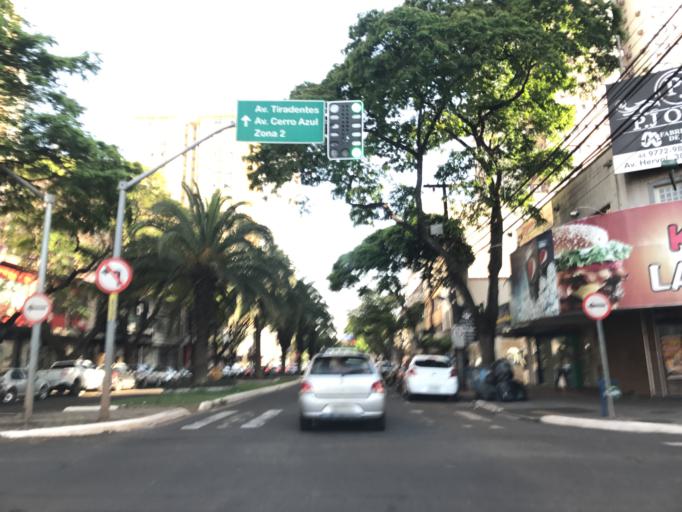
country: BR
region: Parana
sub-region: Maringa
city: Maringa
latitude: -23.4227
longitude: -51.9365
